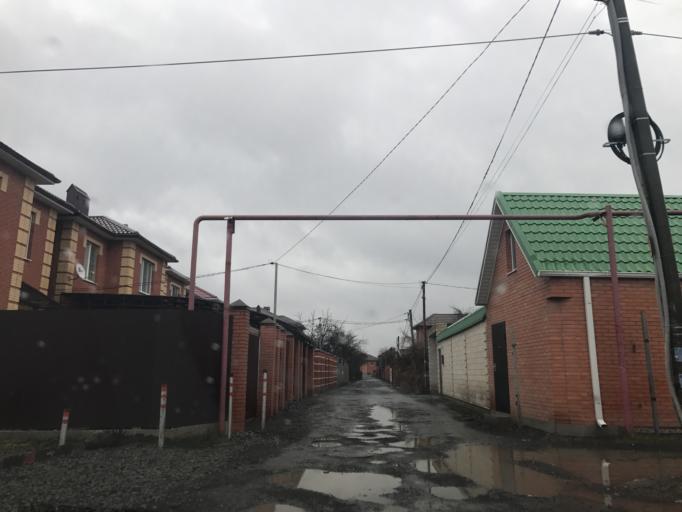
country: RU
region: Rostov
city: Severnyy
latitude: 47.2446
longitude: 39.6192
